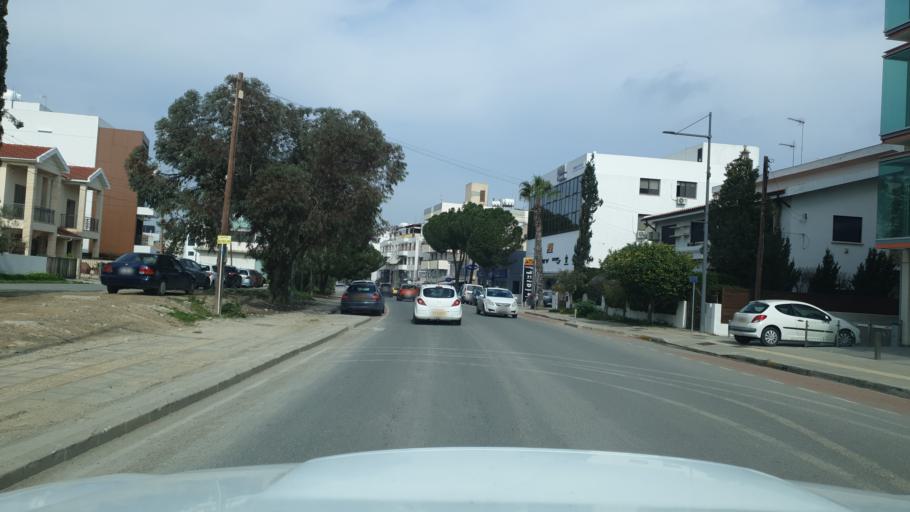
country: CY
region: Lefkosia
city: Nicosia
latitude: 35.1543
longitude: 33.3168
